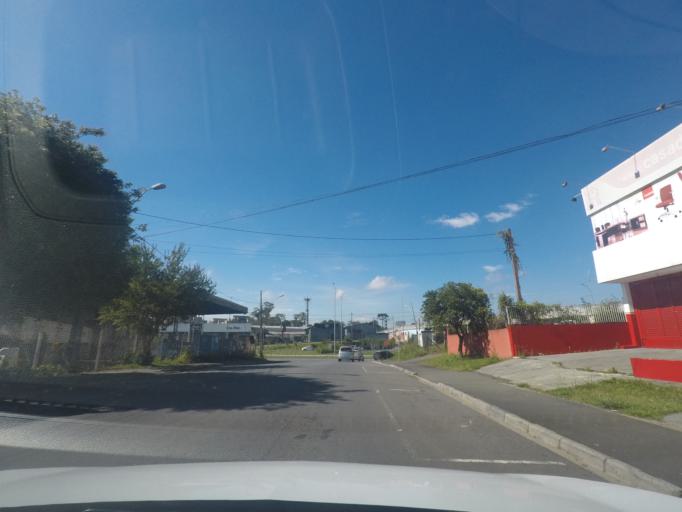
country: BR
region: Parana
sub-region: Curitiba
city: Curitiba
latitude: -25.4951
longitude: -49.2760
